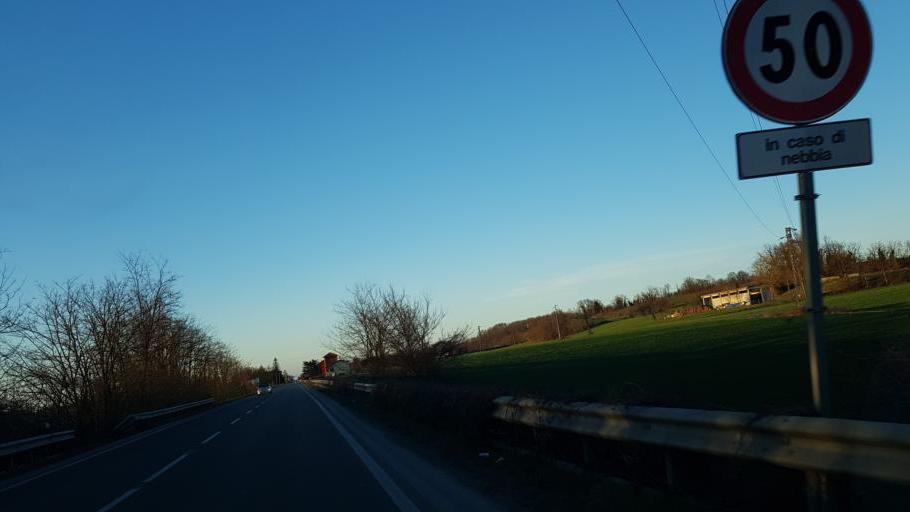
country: IT
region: Piedmont
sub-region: Provincia di Alessandria
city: Villalvernia
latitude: 44.8212
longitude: 8.8545
